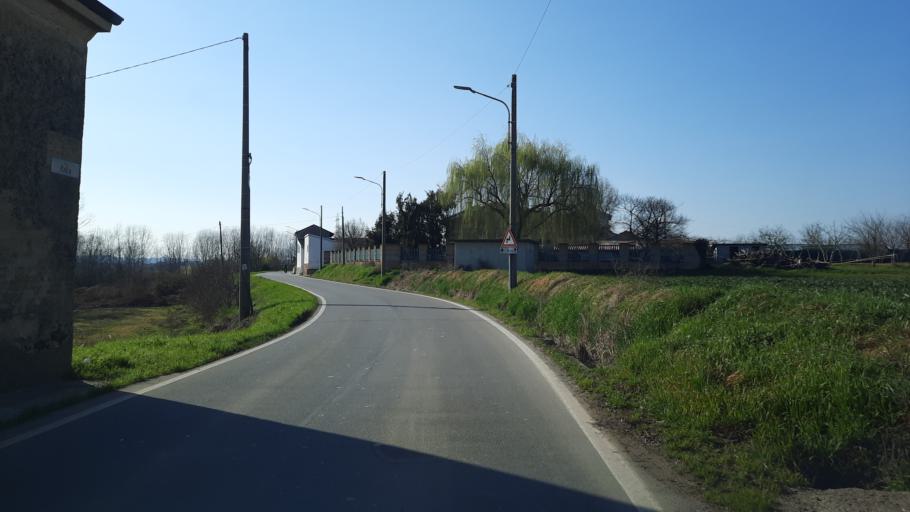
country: IT
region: Piedmont
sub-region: Provincia di Vercelli
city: Trino
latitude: 45.2045
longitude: 8.3237
